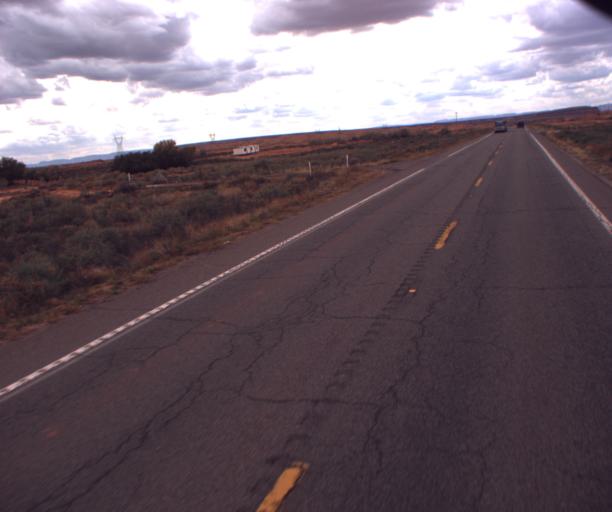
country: US
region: Arizona
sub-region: Navajo County
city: Kayenta
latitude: 36.8288
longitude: -109.8613
